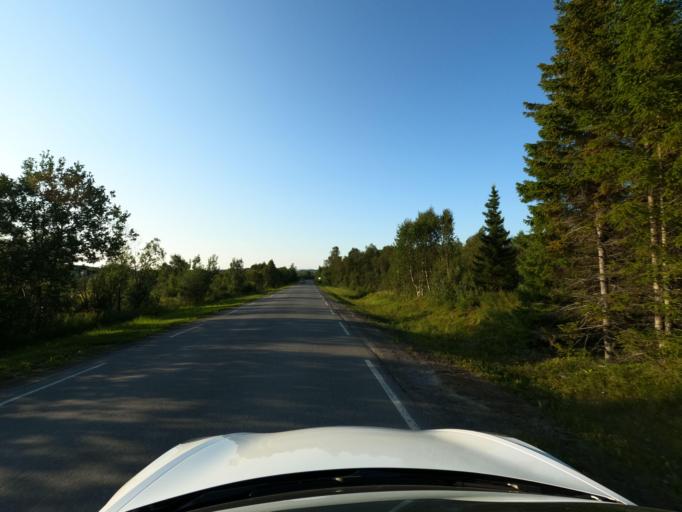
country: NO
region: Troms
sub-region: Skanland
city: Evenskjer
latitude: 68.4816
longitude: 16.7113
